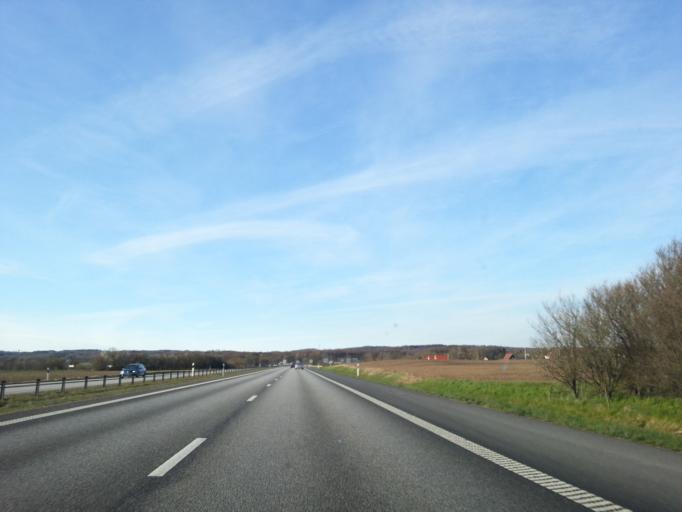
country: SE
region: Skane
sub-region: Angelholms Kommun
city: Munka-Ljungby
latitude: 56.3124
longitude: 12.9110
